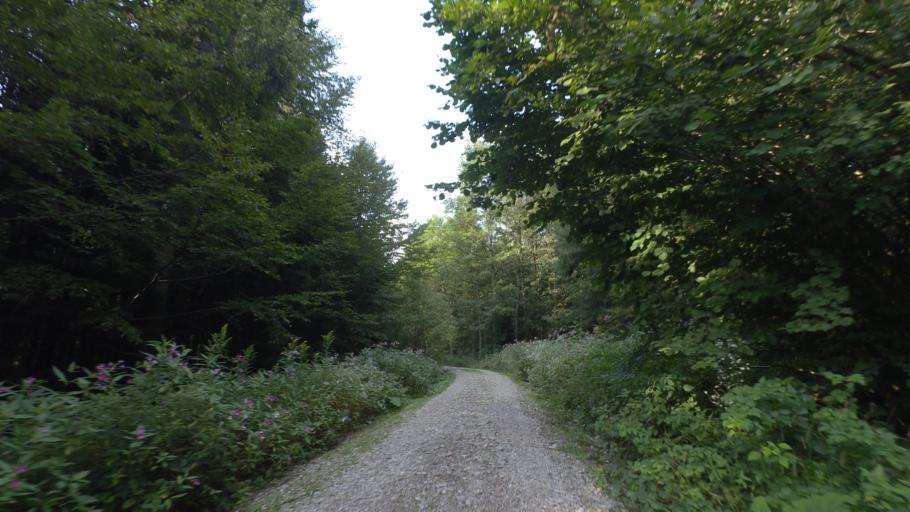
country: DE
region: Bavaria
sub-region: Upper Bavaria
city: Chieming
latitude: 47.9264
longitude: 12.5605
